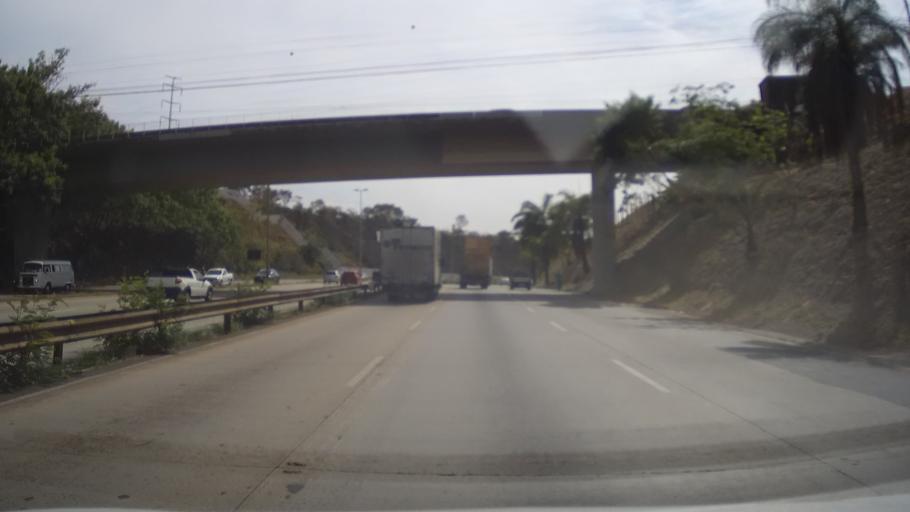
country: BR
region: Minas Gerais
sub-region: Contagem
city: Contagem
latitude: -19.9325
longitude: -44.0192
